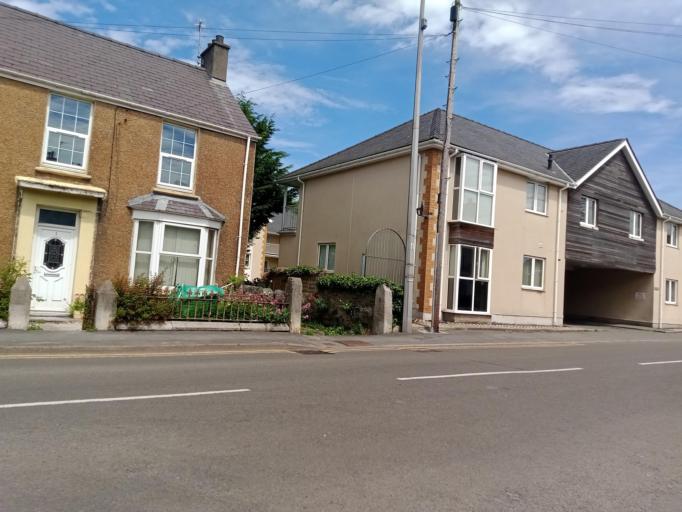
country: GB
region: Wales
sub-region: Anglesey
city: Llanfairpwllgwyngyll
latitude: 53.2212
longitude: -4.2074
